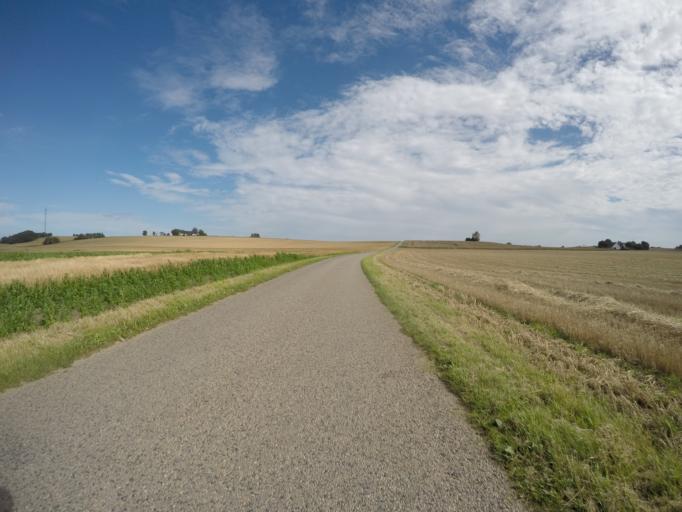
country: SE
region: Skane
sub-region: Simrishamns Kommun
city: Simrishamn
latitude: 55.4955
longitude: 14.2425
